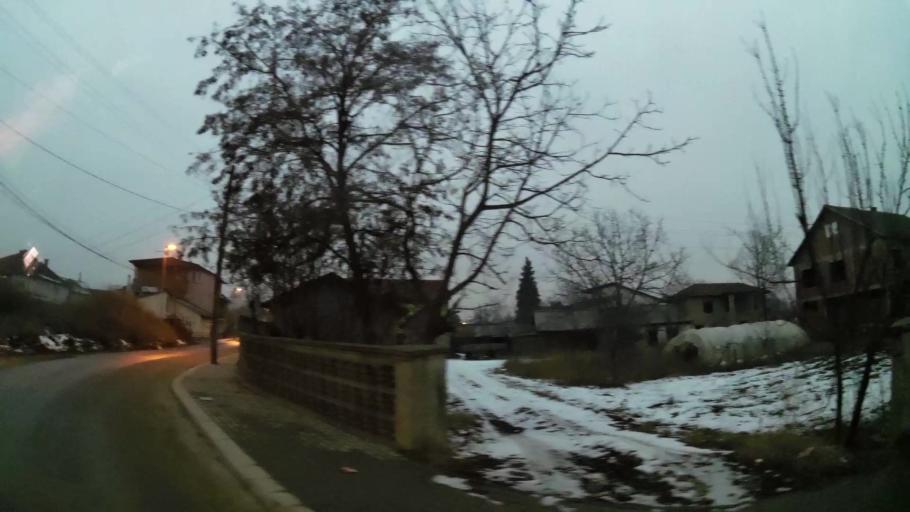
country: MK
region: Kisela Voda
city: Kisela Voda
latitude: 41.9695
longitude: 21.4897
